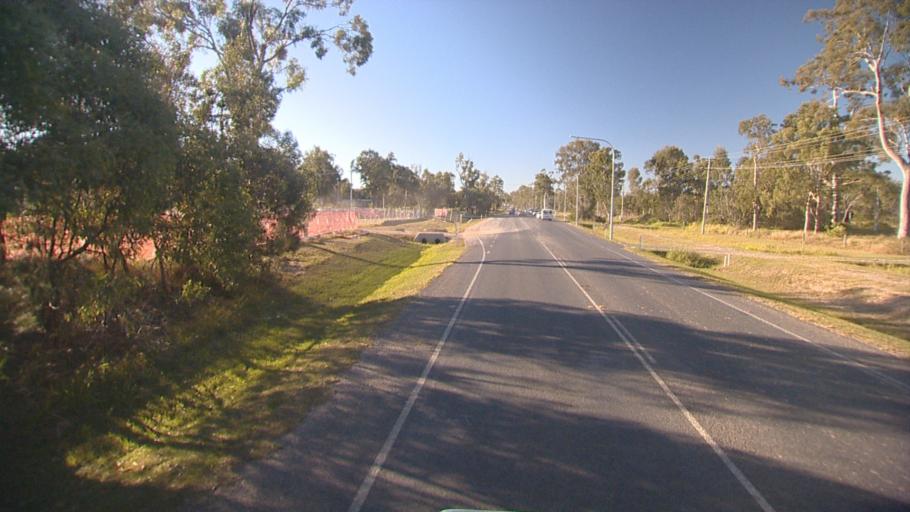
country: AU
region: Queensland
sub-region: Logan
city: Logan Reserve
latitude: -27.7191
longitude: 153.0914
